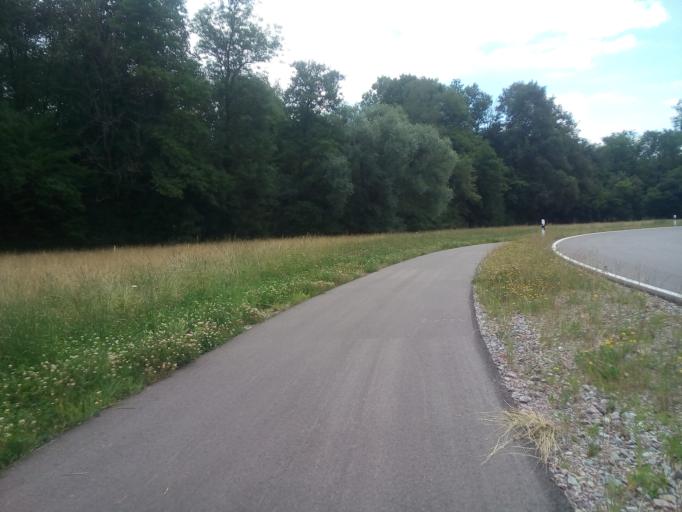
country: DE
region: Baden-Wuerttemberg
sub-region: Freiburg Region
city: Rheinau
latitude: 48.6381
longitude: 7.9466
